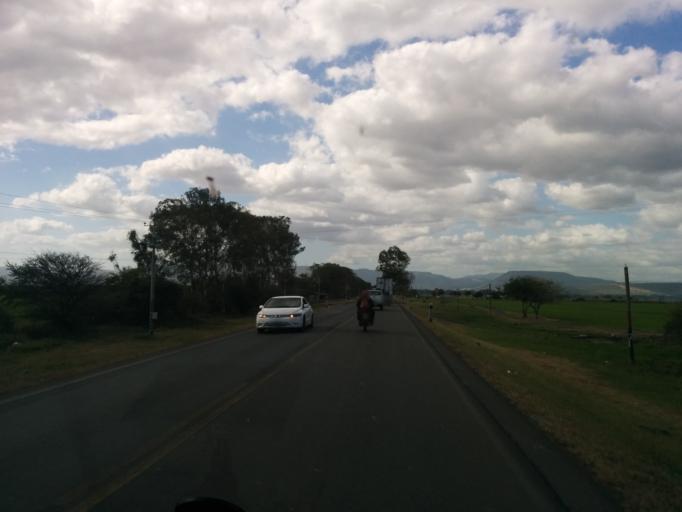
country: NI
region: Matagalpa
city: Ciudad Dario
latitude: 12.8654
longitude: -86.1151
